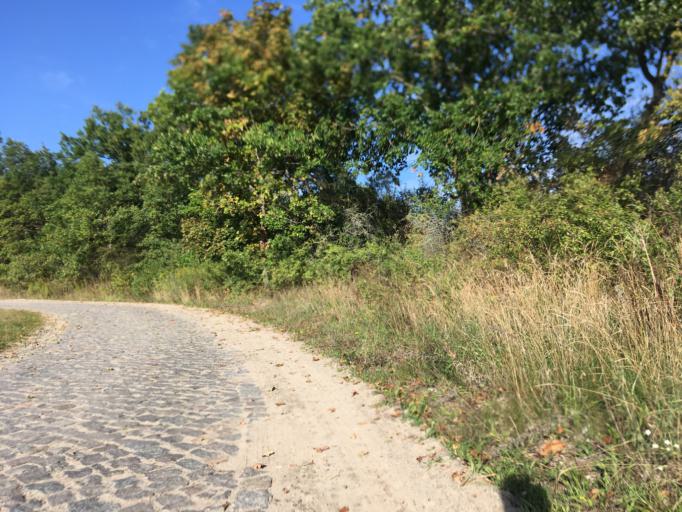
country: DE
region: Brandenburg
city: Neuenhagen
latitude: 52.5213
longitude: 13.7217
